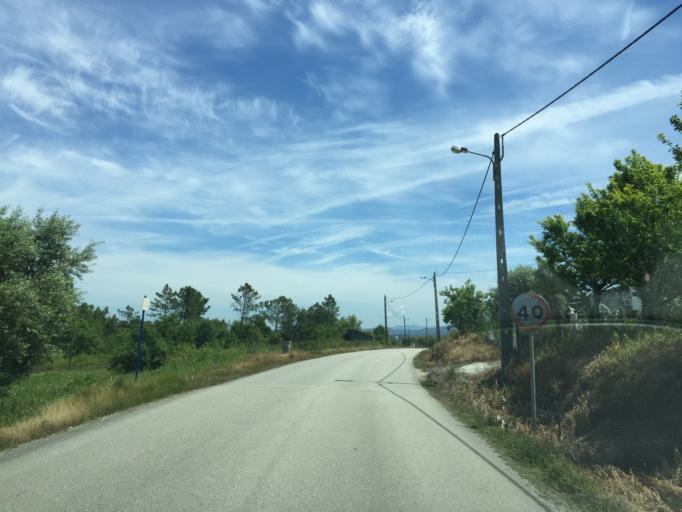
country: PT
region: Coimbra
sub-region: Soure
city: Soure
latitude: 40.0597
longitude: -8.6526
